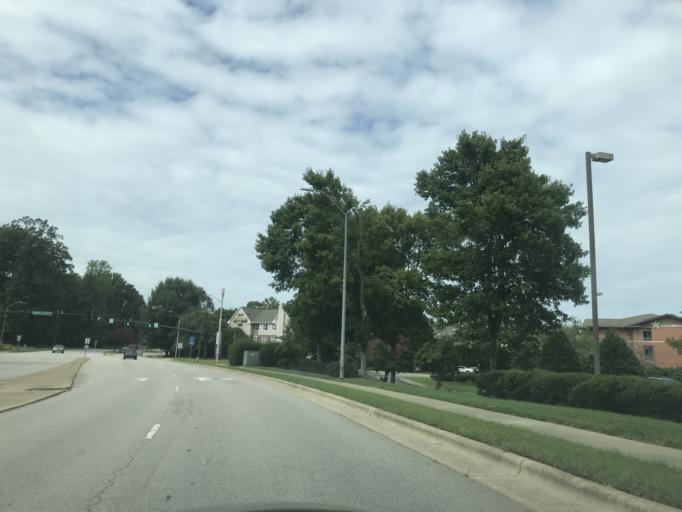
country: US
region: North Carolina
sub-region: Wake County
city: Apex
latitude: 35.7311
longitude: -78.7895
